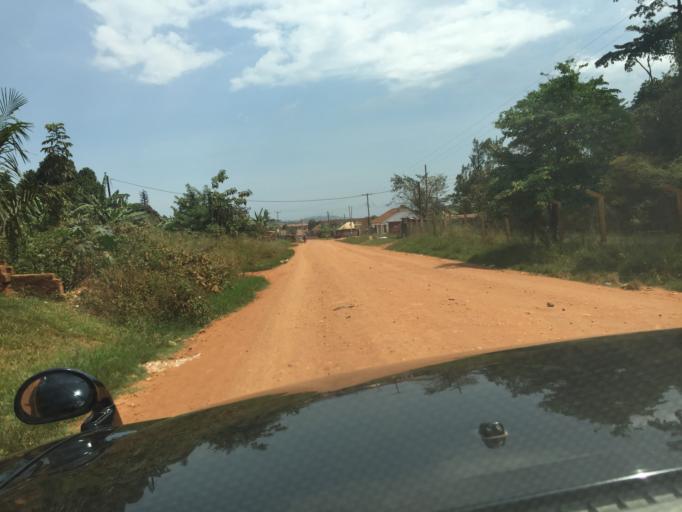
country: UG
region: Central Region
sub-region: Wakiso District
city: Kireka
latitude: 0.4032
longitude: 32.6204
